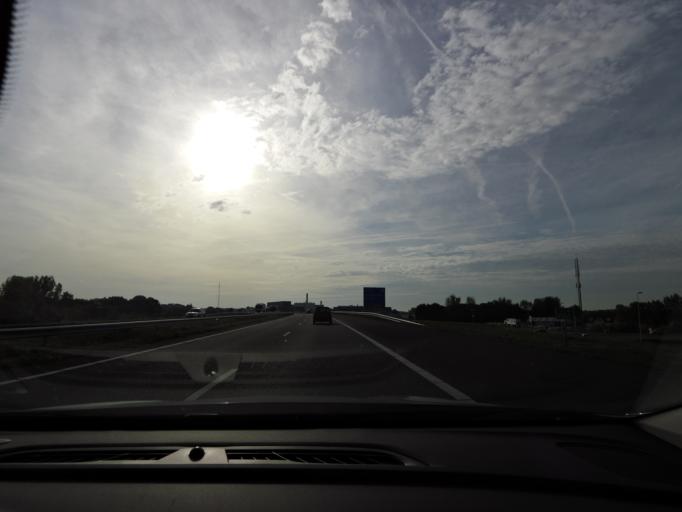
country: NL
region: North Brabant
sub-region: Gemeente Bergen op Zoom
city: Bergen op Zoom
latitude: 51.5105
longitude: 4.3091
